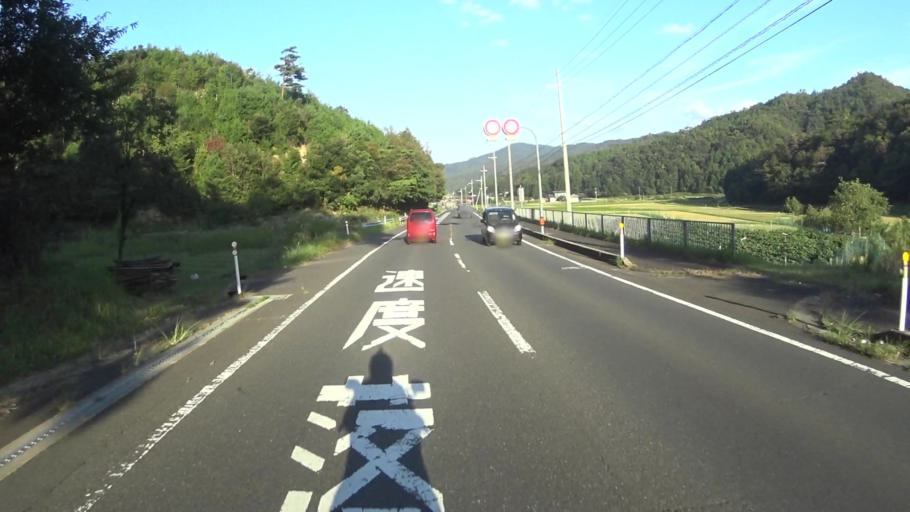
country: JP
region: Kyoto
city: Miyazu
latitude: 35.5780
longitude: 135.0136
